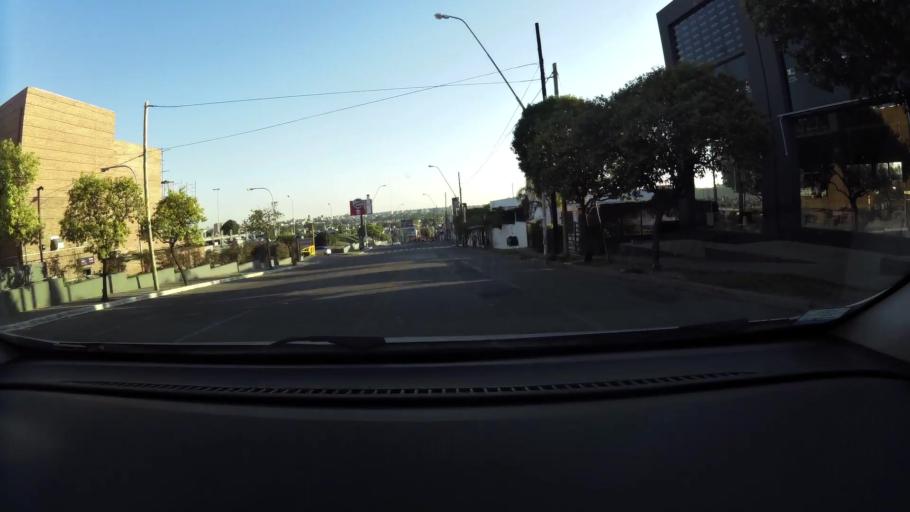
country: AR
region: Cordoba
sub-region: Departamento de Capital
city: Cordoba
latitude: -31.3804
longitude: -64.2156
